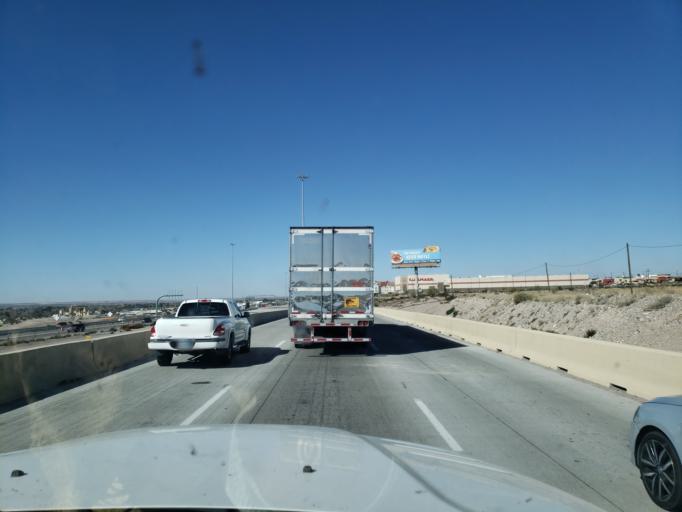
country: US
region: New Mexico
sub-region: Dona Ana County
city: Sunland Park
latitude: 31.8286
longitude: -106.5622
